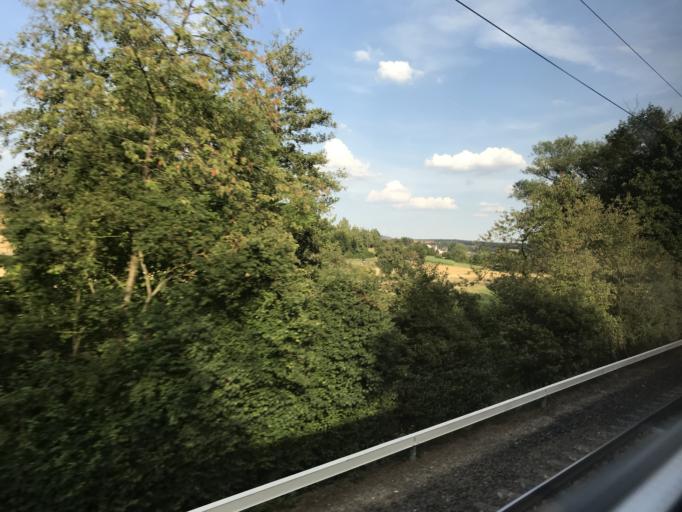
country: DE
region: Hesse
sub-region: Regierungsbezirk Giessen
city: Villmar
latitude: 50.3405
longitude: 8.2139
